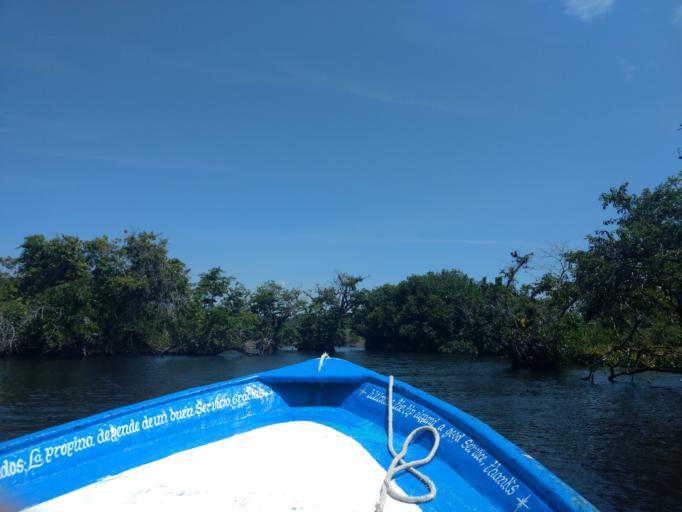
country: MX
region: Nayarit
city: San Blas
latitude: 21.5355
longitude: -105.2369
